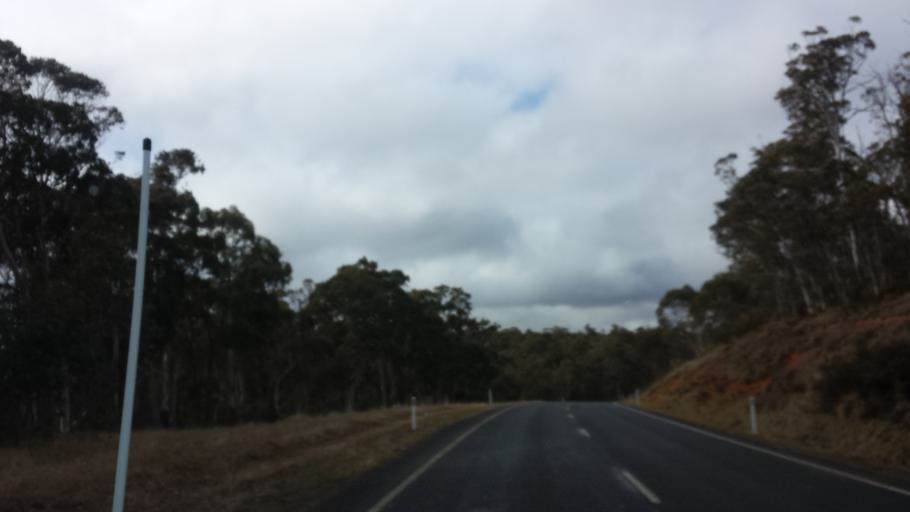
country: AU
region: Victoria
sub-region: Alpine
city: Mount Beauty
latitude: -37.0815
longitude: 147.3650
